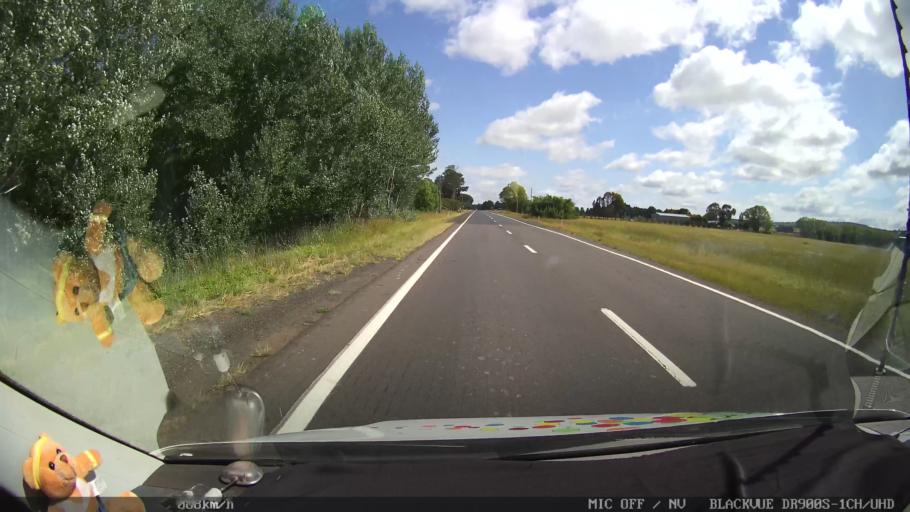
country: AU
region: New South Wales
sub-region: Glen Innes Severn
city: Glen Innes
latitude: -29.8224
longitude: 151.7397
